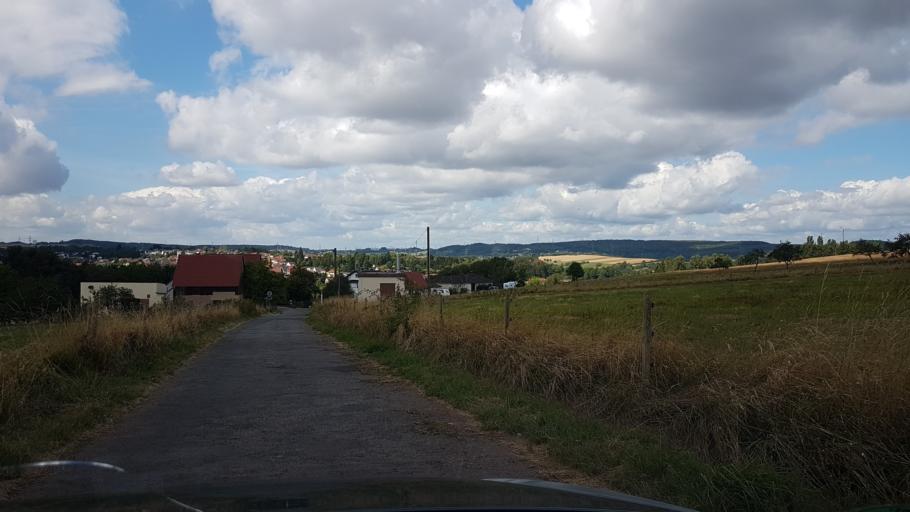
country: DE
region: Saarland
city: Illingen
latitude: 49.3789
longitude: 7.0624
